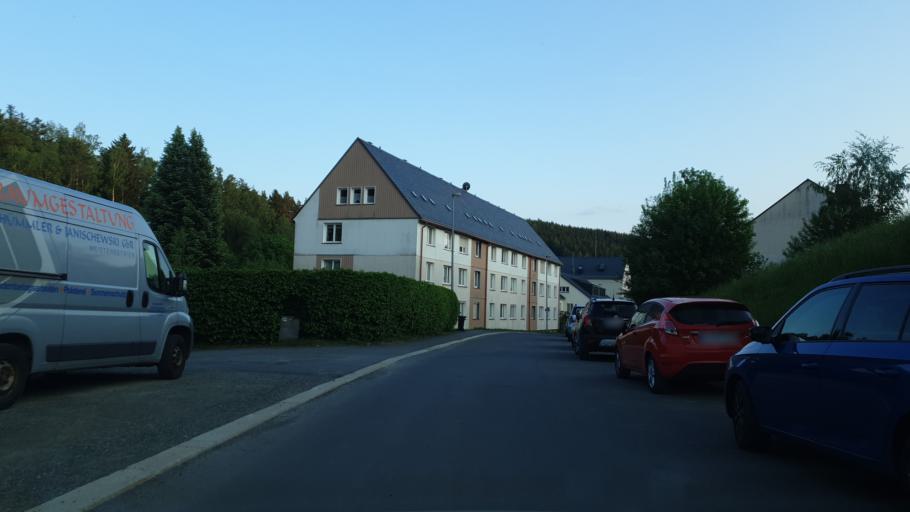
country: DE
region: Saxony
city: Klingenthal
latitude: 50.3615
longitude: 12.4613
